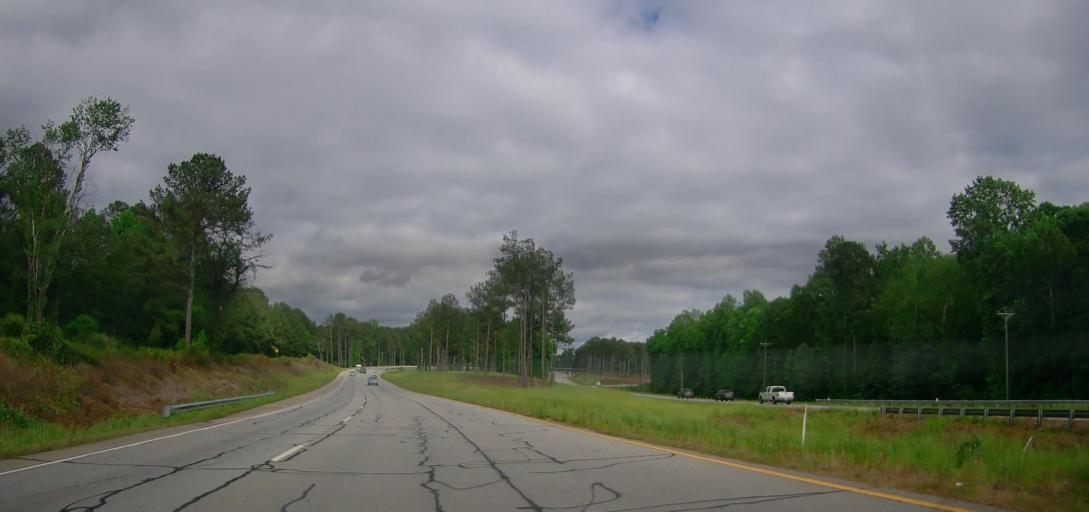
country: US
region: Georgia
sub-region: Walton County
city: Monroe
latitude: 33.8041
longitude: -83.7548
